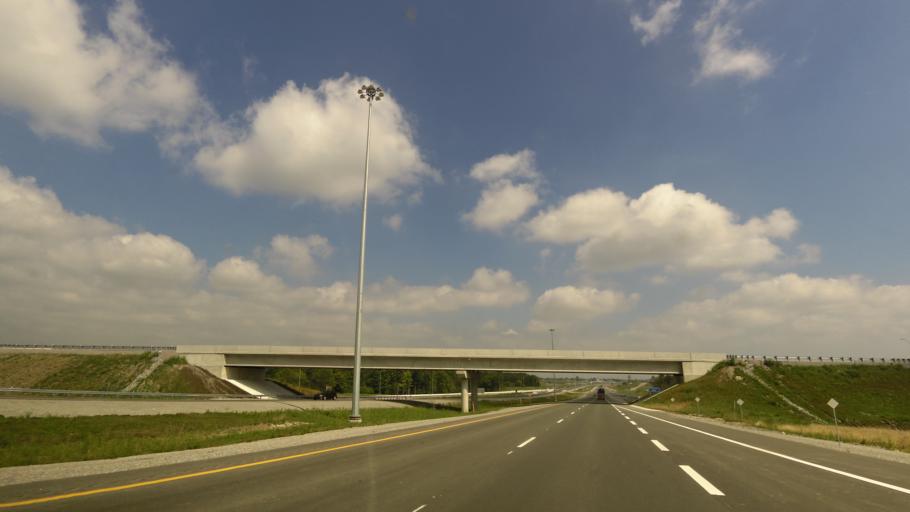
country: CA
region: Ontario
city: Ajax
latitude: 43.9507
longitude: -79.0065
